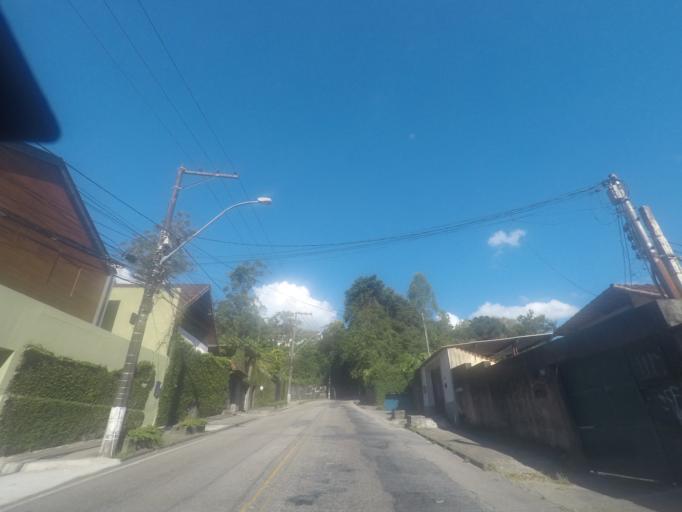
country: BR
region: Rio de Janeiro
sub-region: Petropolis
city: Petropolis
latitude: -22.5264
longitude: -43.1811
